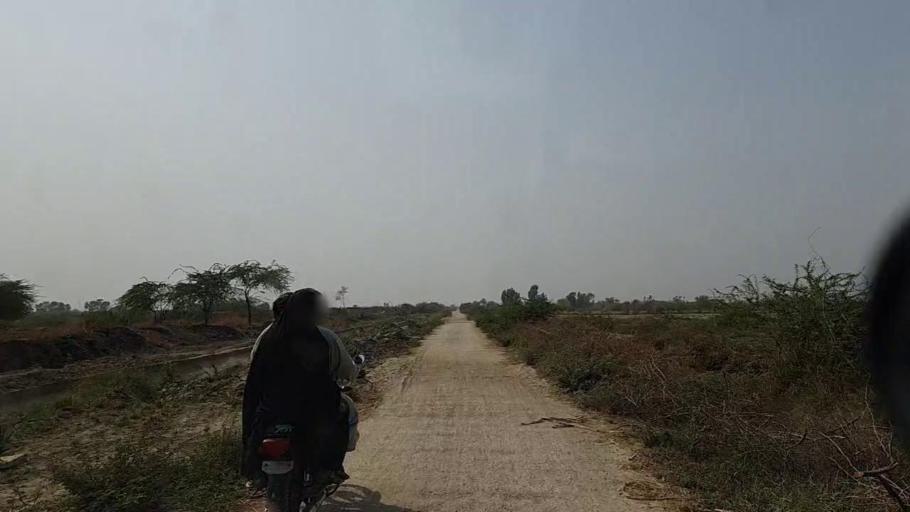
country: PK
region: Sindh
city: Naukot
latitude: 24.7719
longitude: 69.3177
